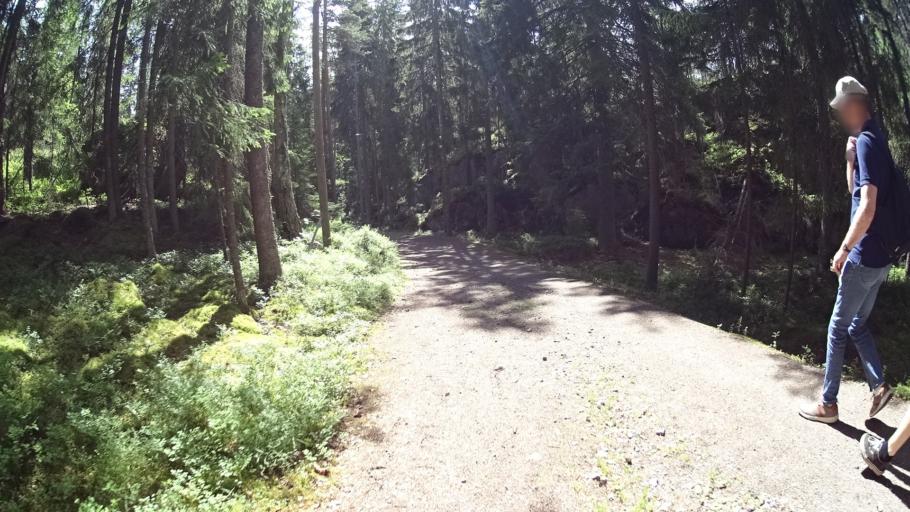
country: FI
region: Uusimaa
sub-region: Helsinki
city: Espoo
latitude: 60.2944
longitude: 24.5711
